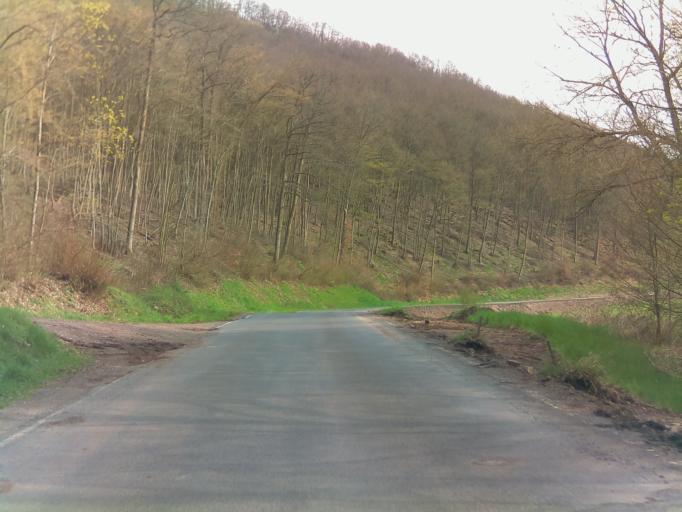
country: DE
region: Rheinland-Pfalz
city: Bockenau
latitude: 49.8446
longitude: 7.6648
